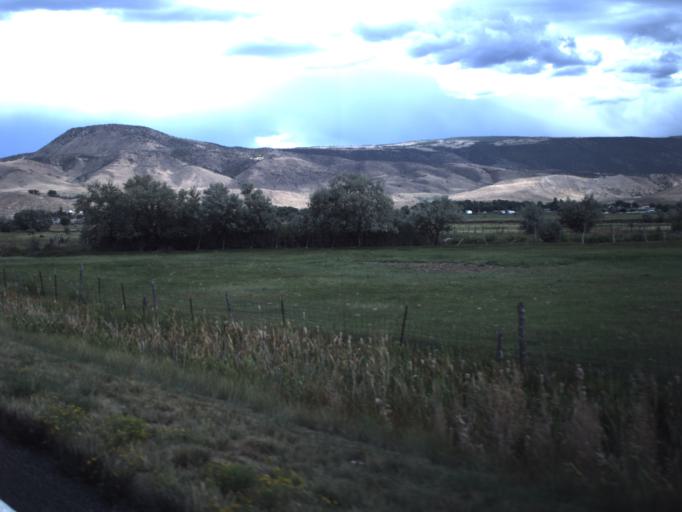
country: US
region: Utah
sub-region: Sevier County
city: Richfield
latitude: 38.7743
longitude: -112.0076
